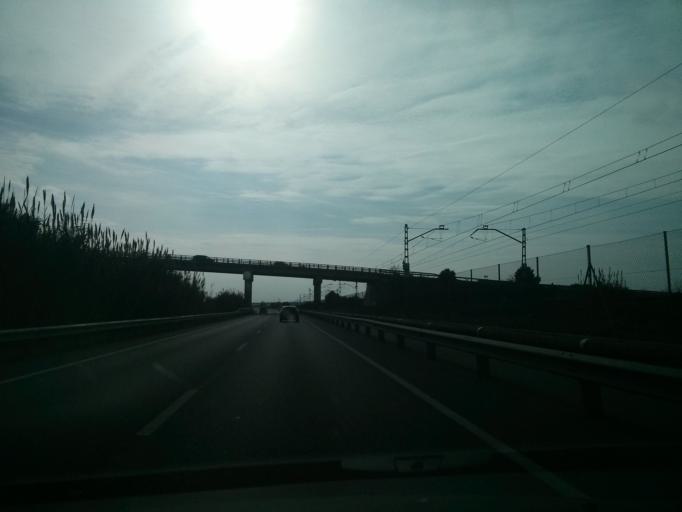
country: ES
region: Catalonia
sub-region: Provincia de Tarragona
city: El Vendrell
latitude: 41.2092
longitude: 1.5347
